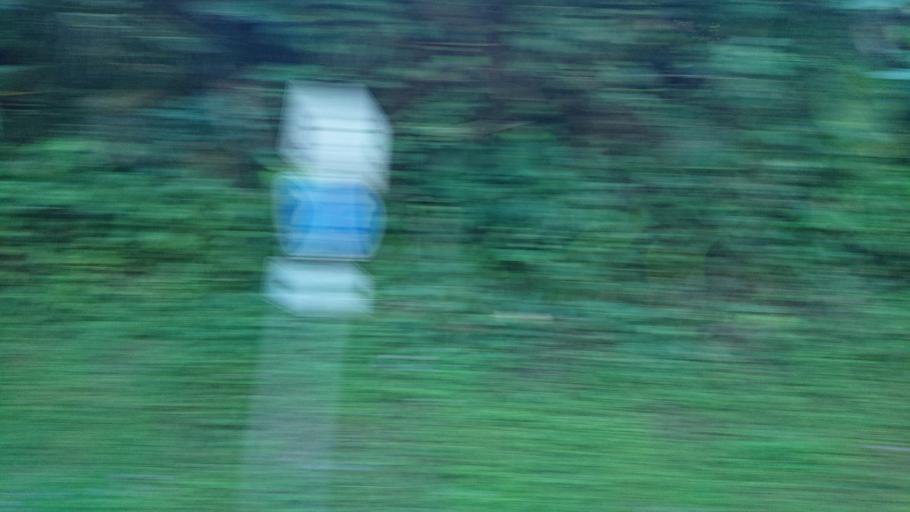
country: TW
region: Taiwan
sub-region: Yilan
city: Yilan
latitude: 24.5774
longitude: 121.4903
